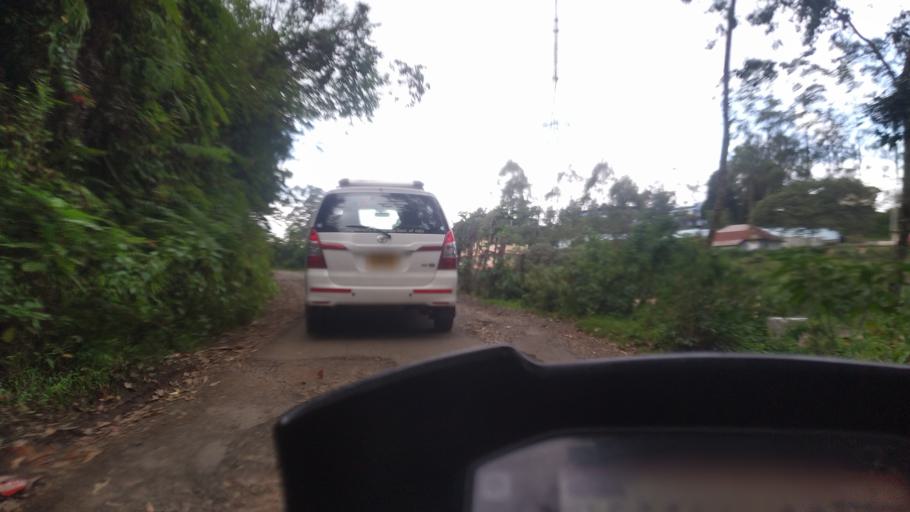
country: IN
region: Kerala
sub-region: Idukki
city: Munnar
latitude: 10.0634
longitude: 77.1075
